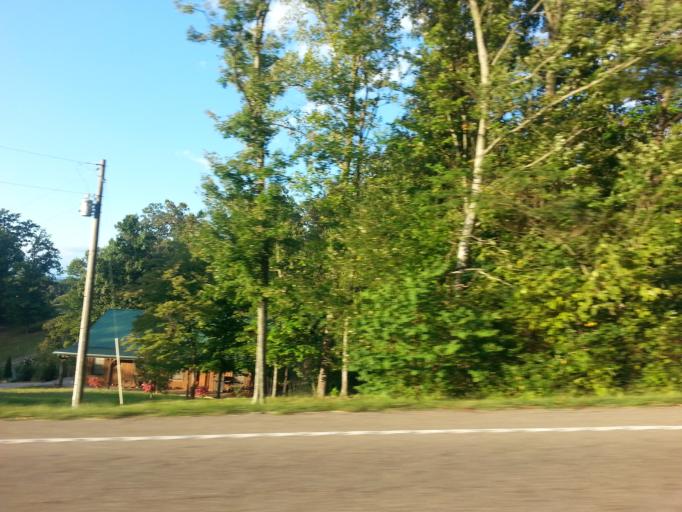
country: US
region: Tennessee
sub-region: Jefferson County
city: Jefferson City
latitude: 36.1318
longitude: -83.5222
